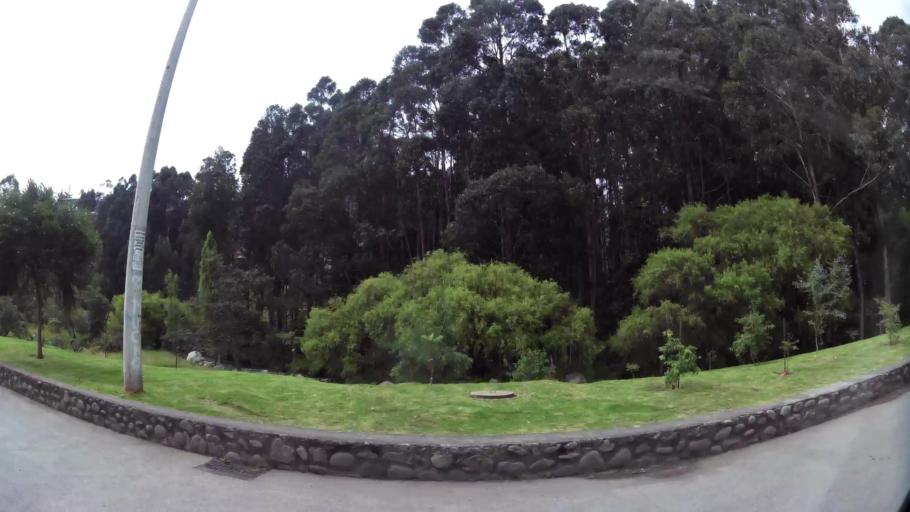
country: EC
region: Azuay
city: Cuenca
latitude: -2.9173
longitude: -79.0122
